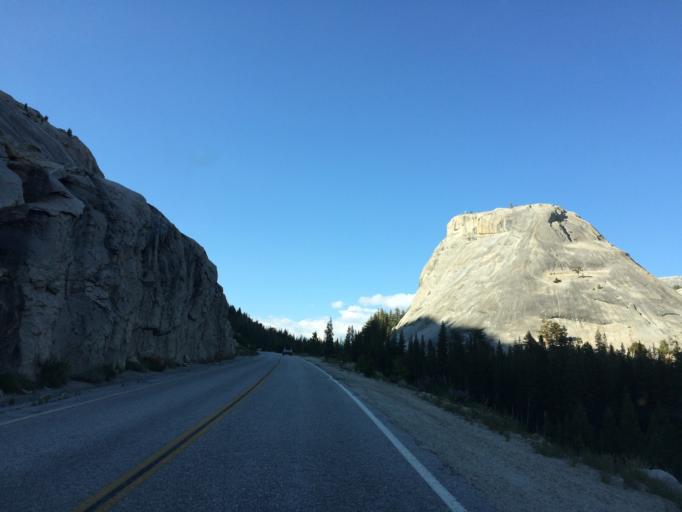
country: US
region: California
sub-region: Mariposa County
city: Yosemite Valley
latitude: 37.8423
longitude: -119.4481
